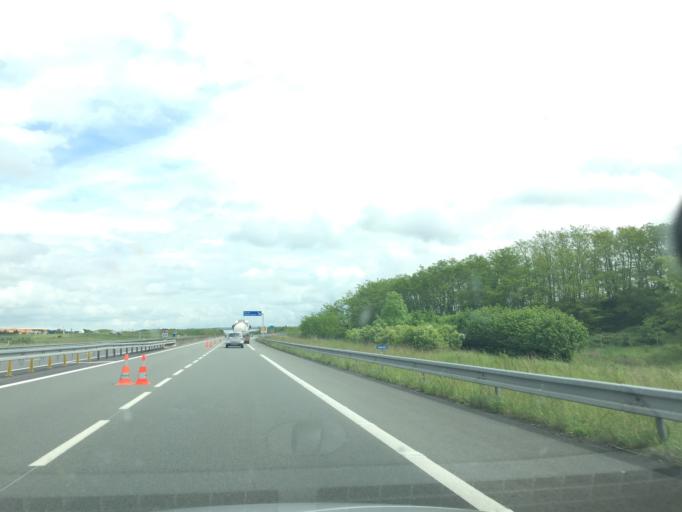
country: FR
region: Centre
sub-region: Departement d'Indre-et-Loire
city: Saint-Christophe-sur-le-Nais
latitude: 47.6505
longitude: 0.4606
